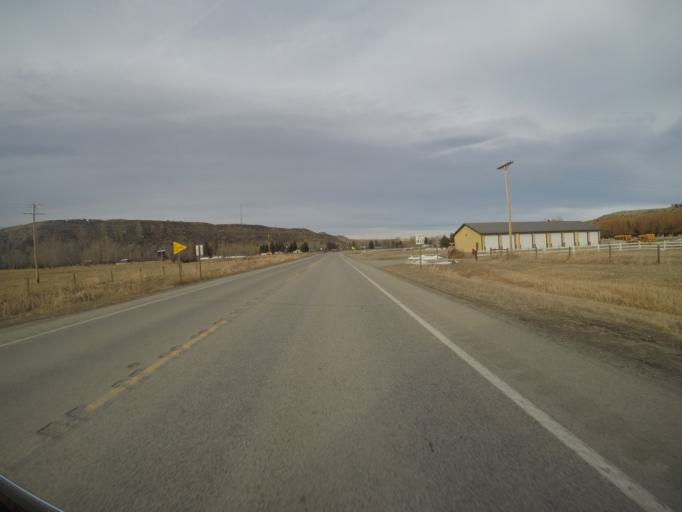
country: US
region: Montana
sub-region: Stillwater County
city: Absarokee
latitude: 45.5119
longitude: -109.4486
